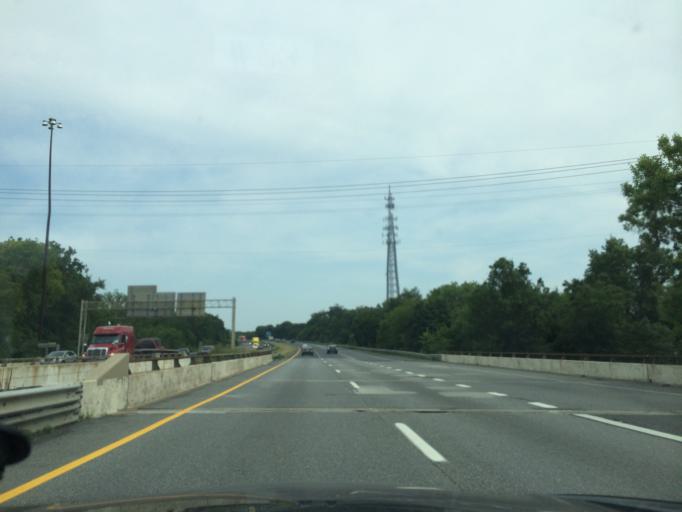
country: US
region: Maryland
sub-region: Washington County
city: Halfway
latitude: 39.6131
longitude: -77.7830
